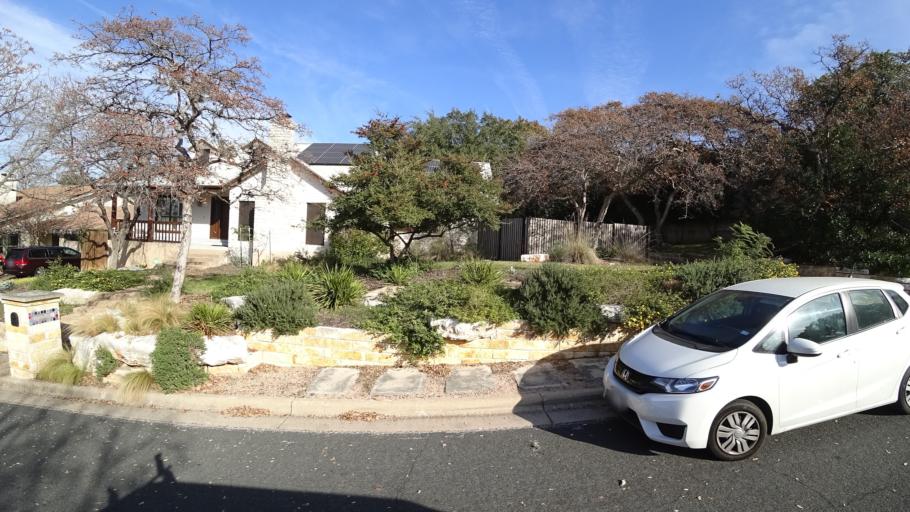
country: US
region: Texas
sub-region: Williamson County
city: Jollyville
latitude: 30.3803
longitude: -97.7579
